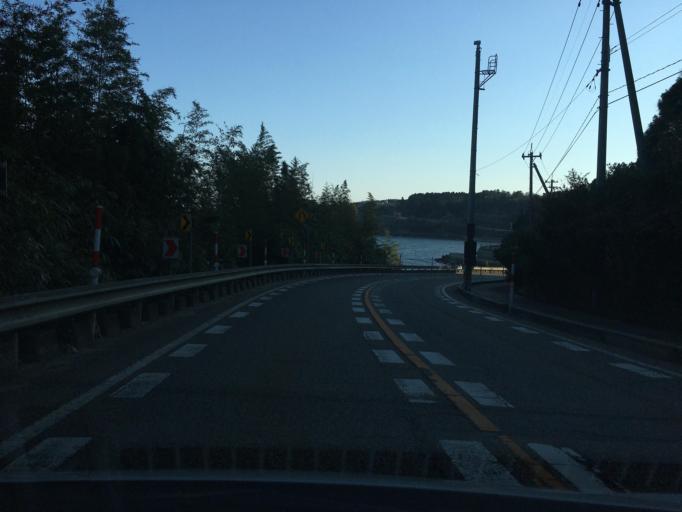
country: JP
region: Ishikawa
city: Nanao
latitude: 36.9912
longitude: 137.0525
